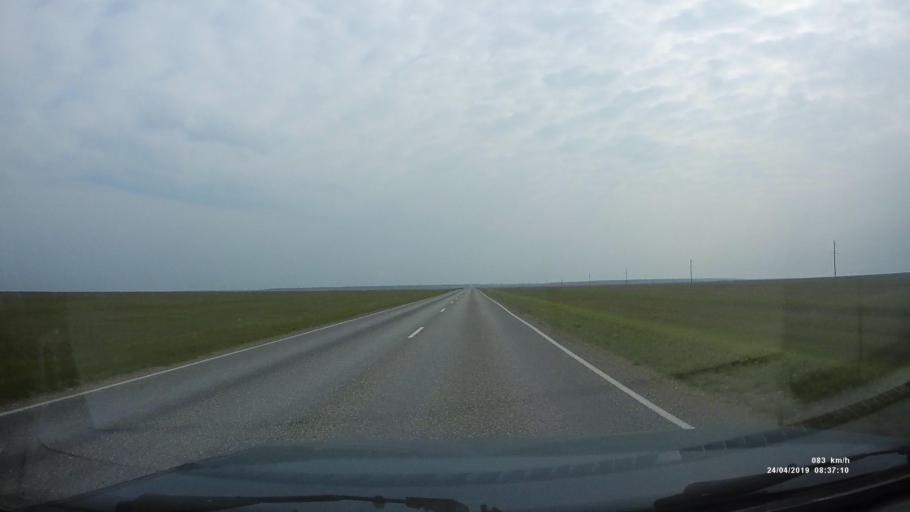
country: RU
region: Kalmykiya
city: Arshan'
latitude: 46.2086
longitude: 43.9466
